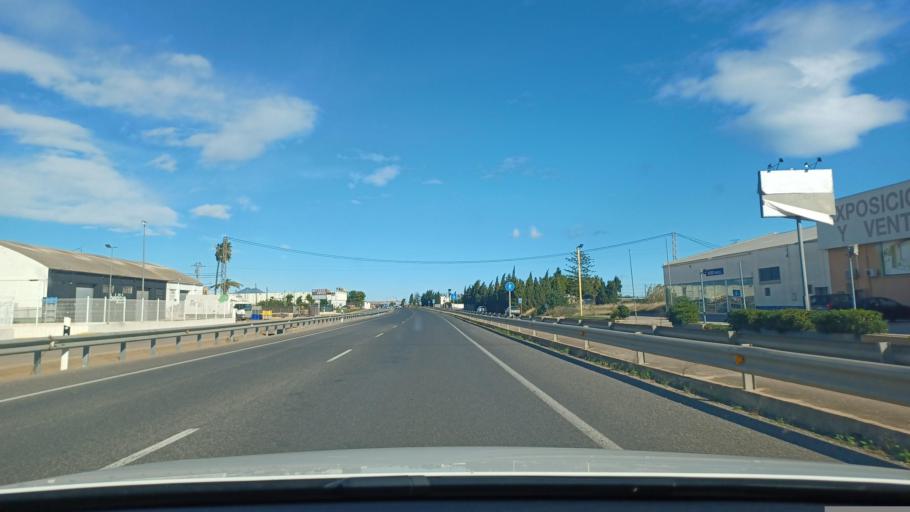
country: ES
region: Valencia
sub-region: Provincia de Castello
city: Benicarlo
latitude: 40.4271
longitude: 0.4335
